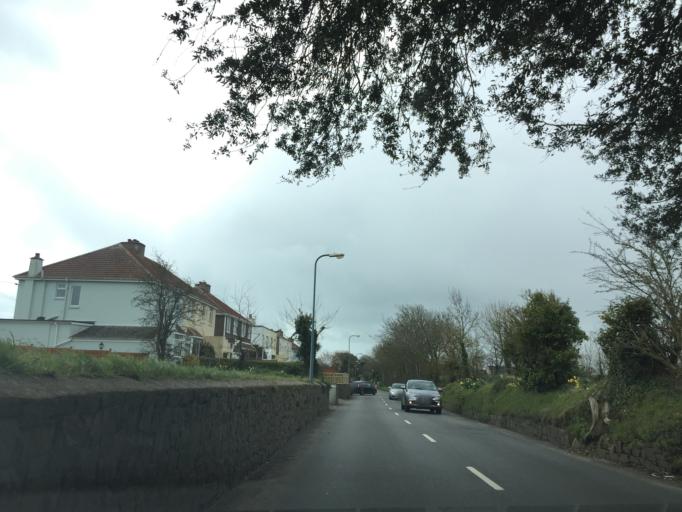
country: JE
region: St Helier
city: Saint Helier
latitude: 49.2104
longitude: -2.1419
